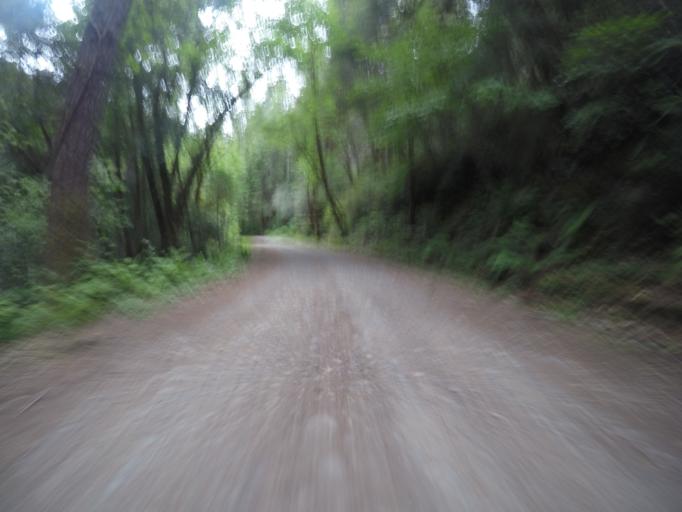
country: US
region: California
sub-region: Del Norte County
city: Bertsch-Oceanview
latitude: 41.7353
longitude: -123.8815
